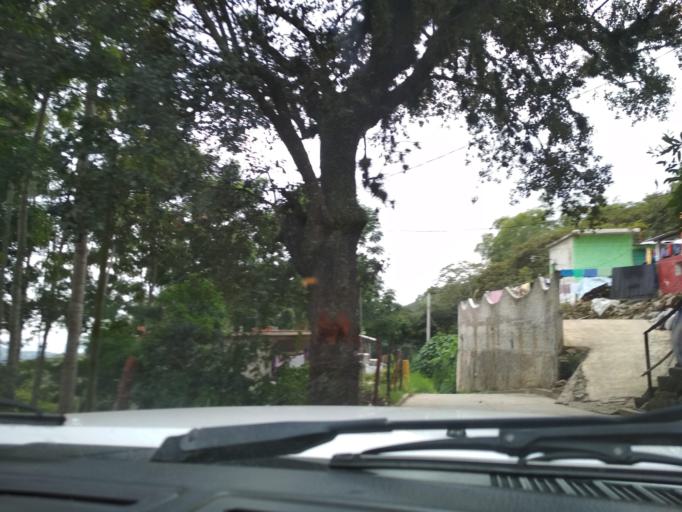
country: MX
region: Veracruz
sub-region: Naolinco
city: El Espinal
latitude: 19.5903
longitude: -96.8798
